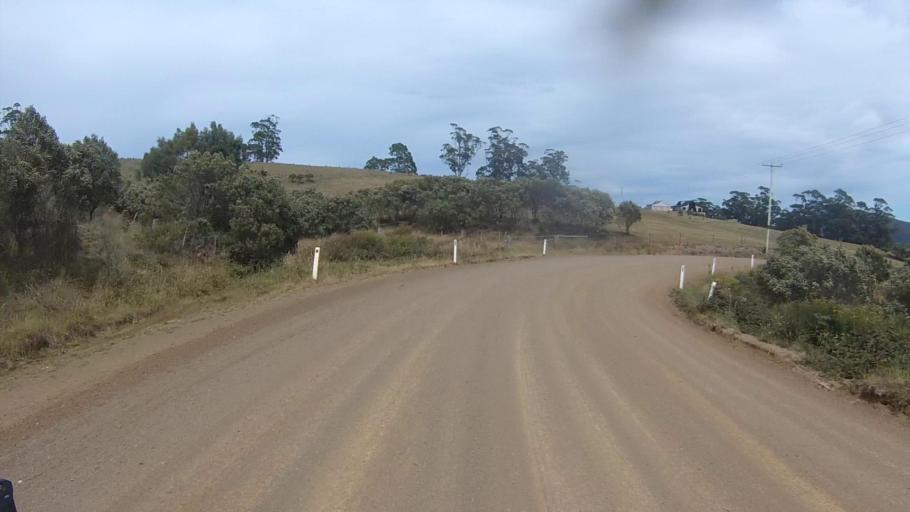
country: AU
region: Tasmania
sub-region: Sorell
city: Sorell
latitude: -42.7777
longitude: 147.8254
